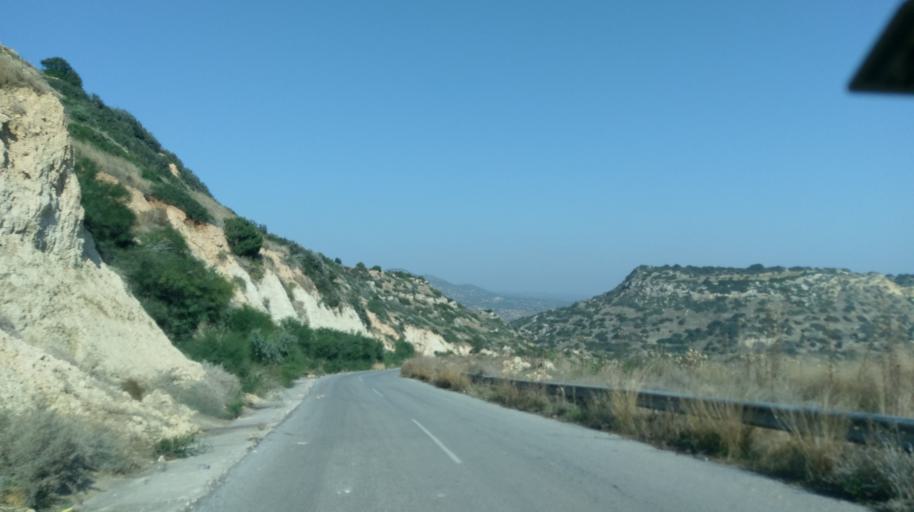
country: CY
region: Ammochostos
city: Leonarisso
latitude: 35.4913
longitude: 34.2231
